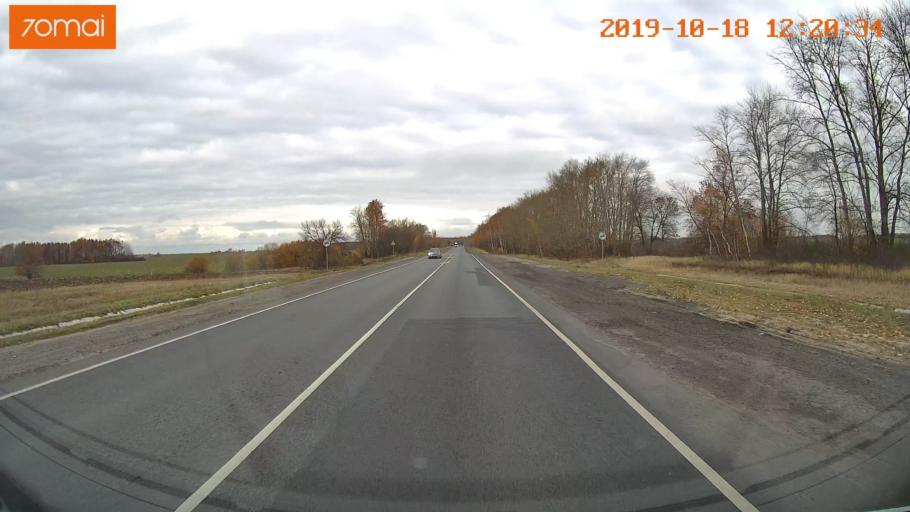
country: RU
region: Rjazan
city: Bagramovo
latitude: 54.5004
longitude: 39.4825
